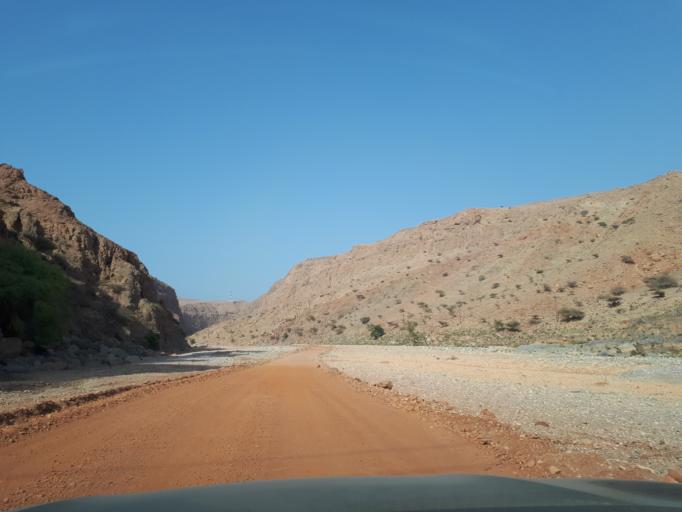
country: OM
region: Ash Sharqiyah
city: Al Qabil
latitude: 23.0690
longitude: 59.0105
